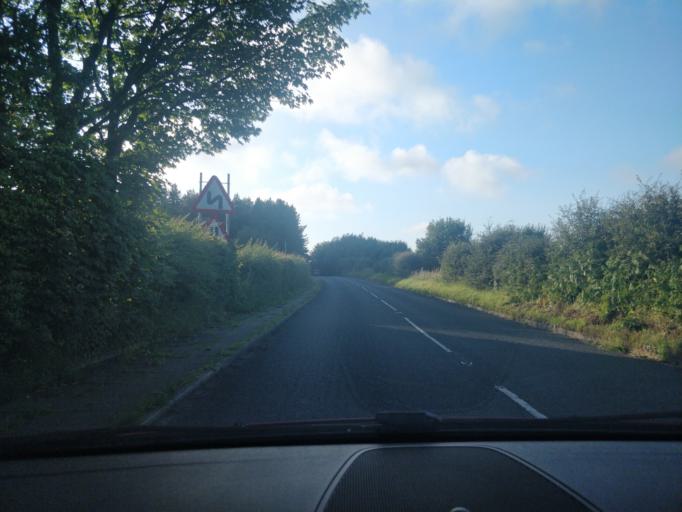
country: GB
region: England
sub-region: Lancashire
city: Skelmersdale
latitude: 53.5511
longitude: -2.7416
